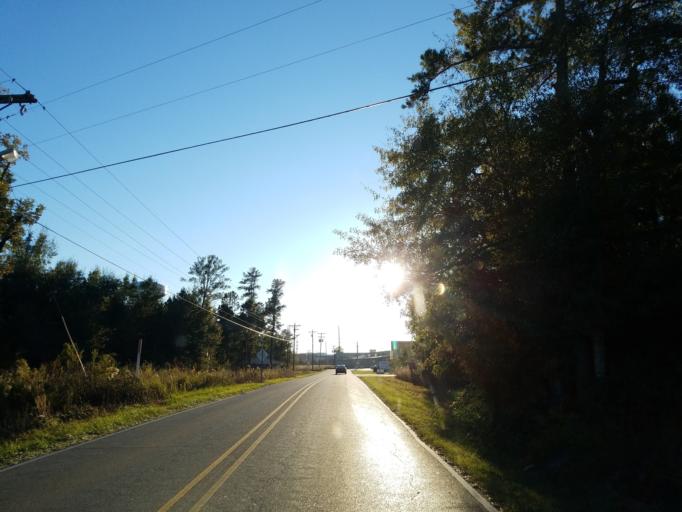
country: US
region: Mississippi
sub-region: Lamar County
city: Arnold Line
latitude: 31.3309
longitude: -89.3703
